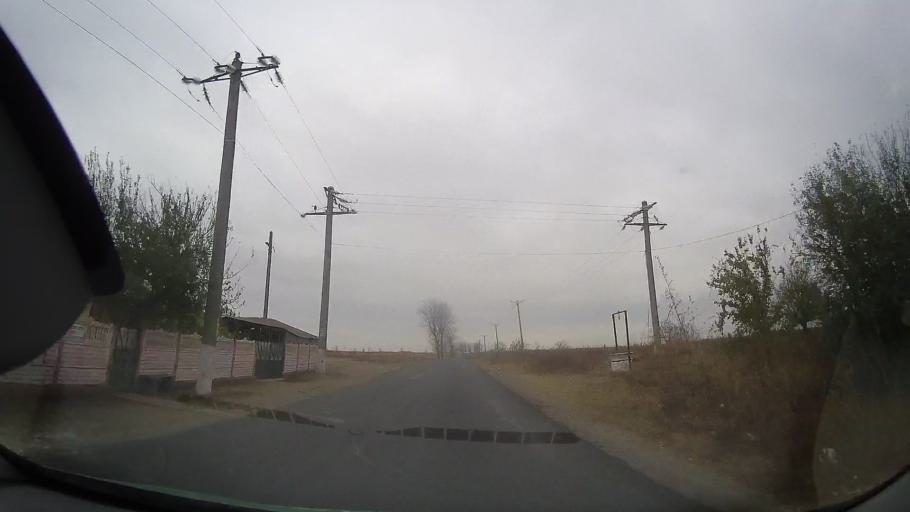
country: RO
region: Braila
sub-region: Comuna Ciresu
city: Ciresu
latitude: 44.9404
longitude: 27.3576
